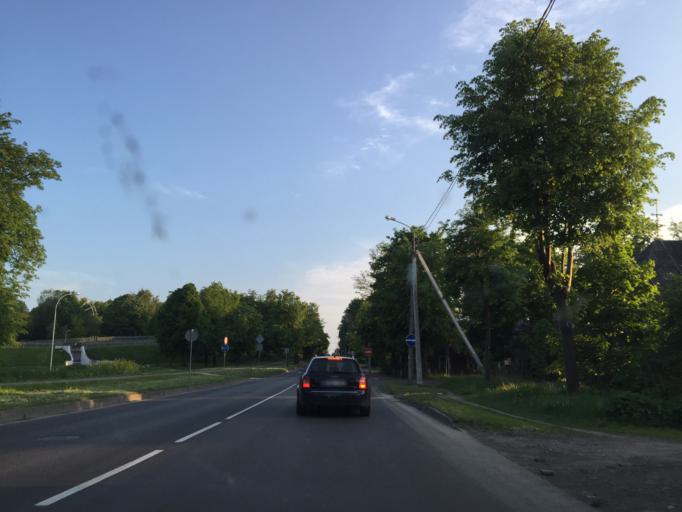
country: LT
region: Siauliu apskritis
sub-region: Siauliai
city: Siauliai
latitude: 55.9419
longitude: 23.3135
